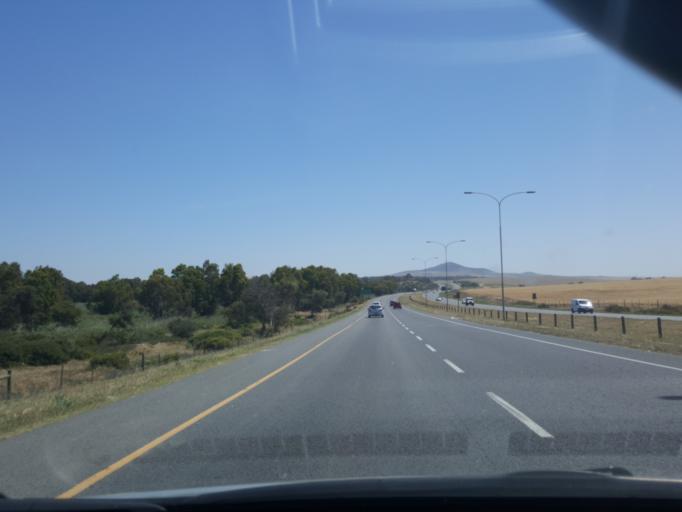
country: ZA
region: Western Cape
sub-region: City of Cape Town
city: Sunset Beach
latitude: -33.7980
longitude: 18.5476
